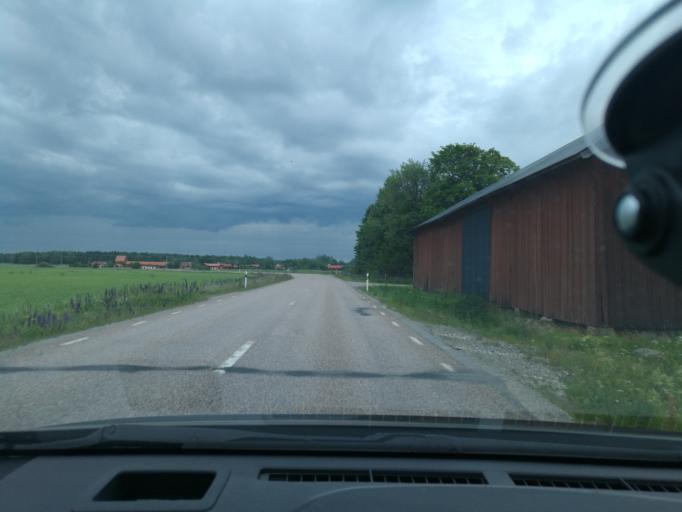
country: SE
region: Vaestmanland
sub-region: Sala Kommun
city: Sala
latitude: 59.9158
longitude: 16.4933
